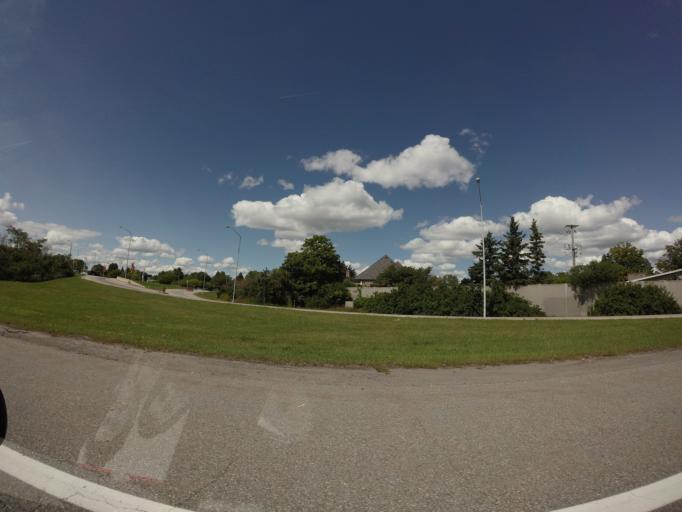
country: CA
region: Ontario
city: Bells Corners
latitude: 45.3619
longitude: -75.7674
